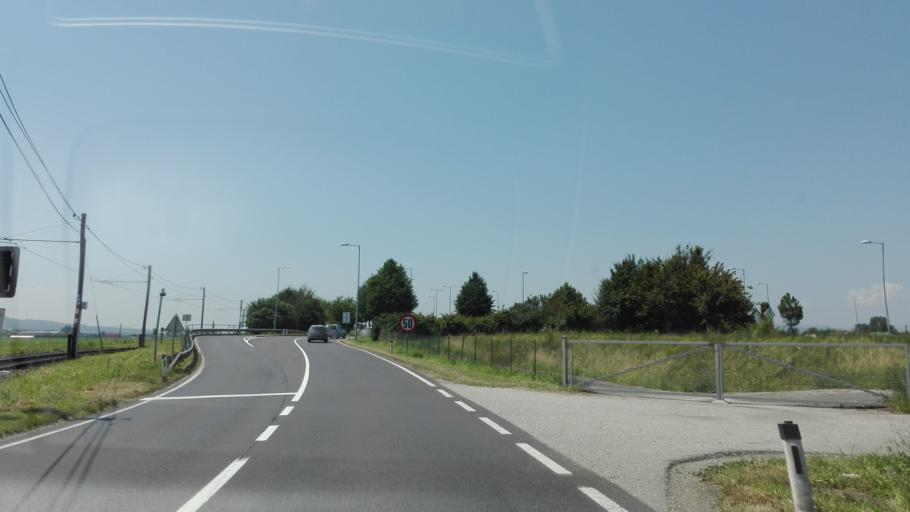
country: AT
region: Upper Austria
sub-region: Politischer Bezirk Urfahr-Umgebung
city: Goldworth
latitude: 48.2889
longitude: 14.1320
